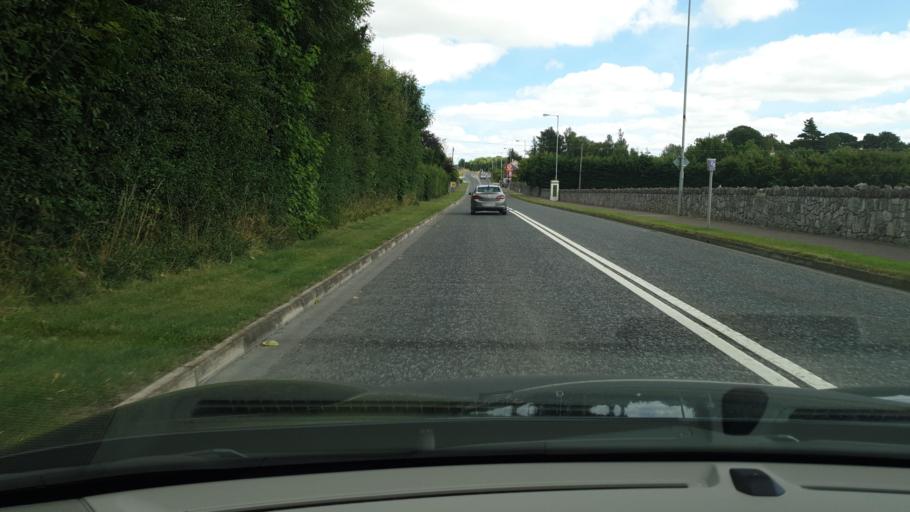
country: IE
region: Leinster
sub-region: An Mhi
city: Newtown Trim
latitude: 53.5267
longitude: -6.6748
